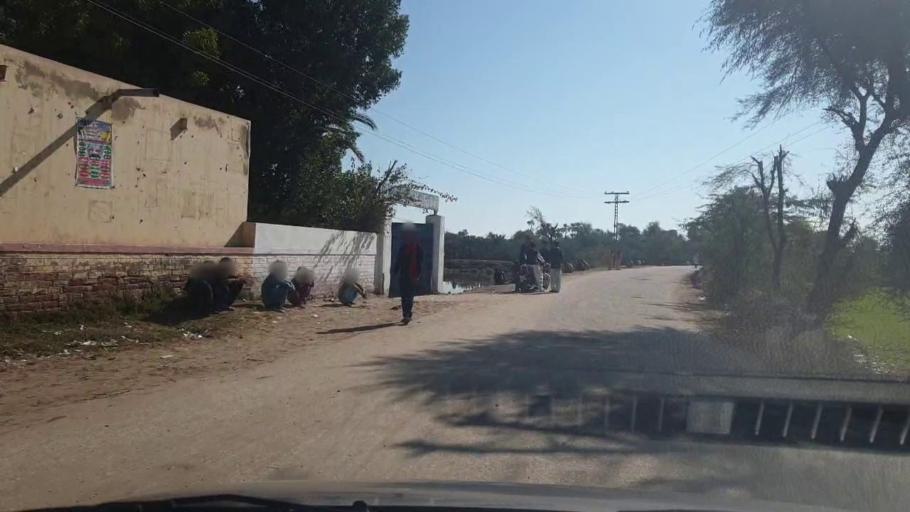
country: PK
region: Sindh
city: Bozdar
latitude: 27.1208
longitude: 68.6331
